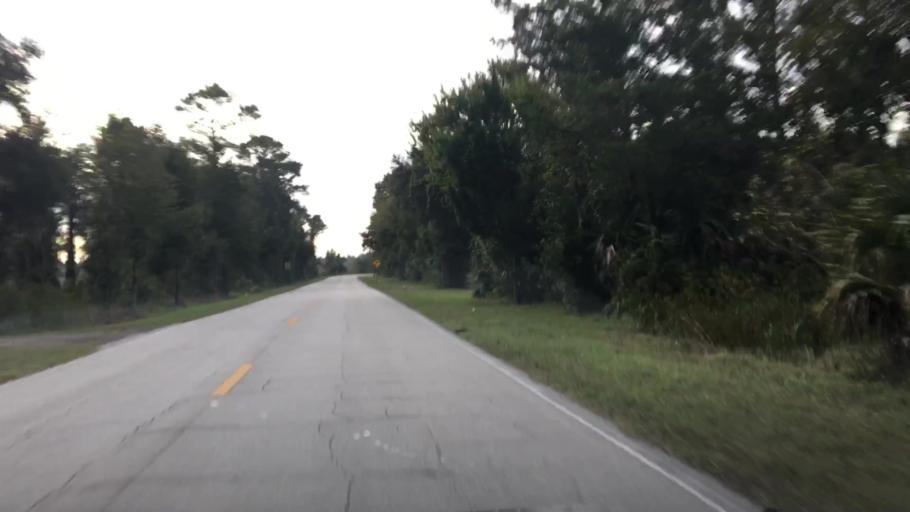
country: US
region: Florida
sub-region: Seminole County
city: Midway
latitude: 28.8423
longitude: -81.1969
